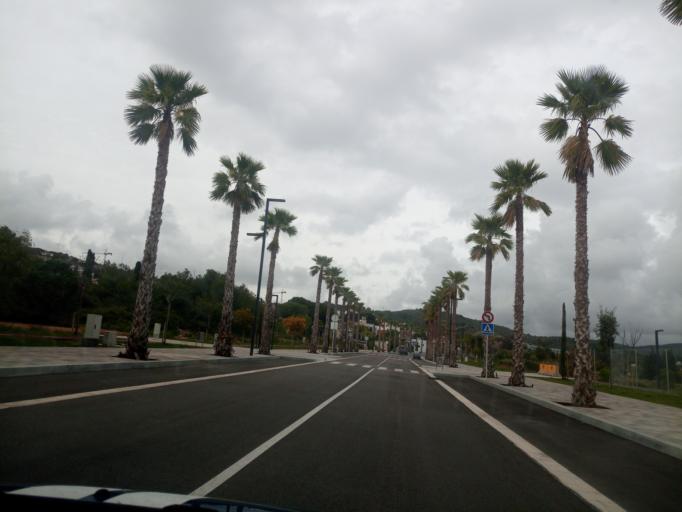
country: ES
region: Catalonia
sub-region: Provincia de Barcelona
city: Sitges
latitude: 41.2428
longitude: 1.7997
